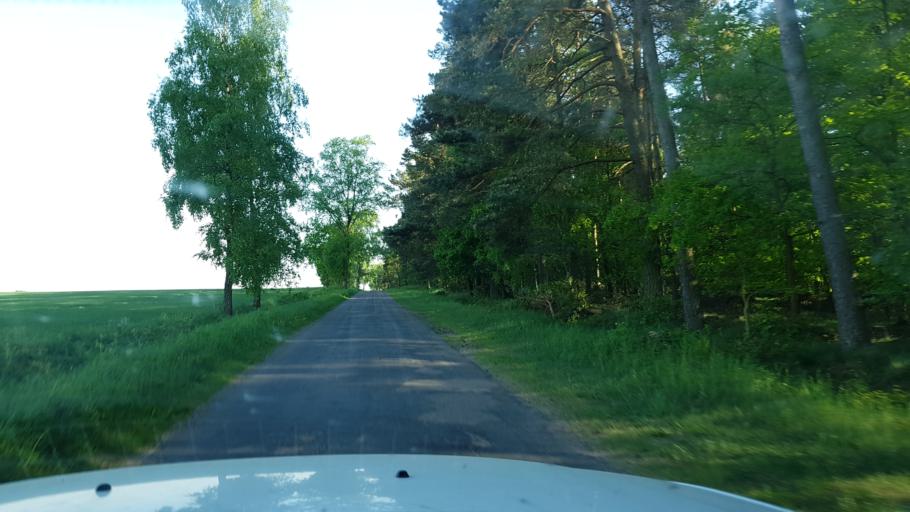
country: PL
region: West Pomeranian Voivodeship
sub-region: Powiat lobeski
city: Dobra
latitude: 53.6063
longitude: 15.3304
